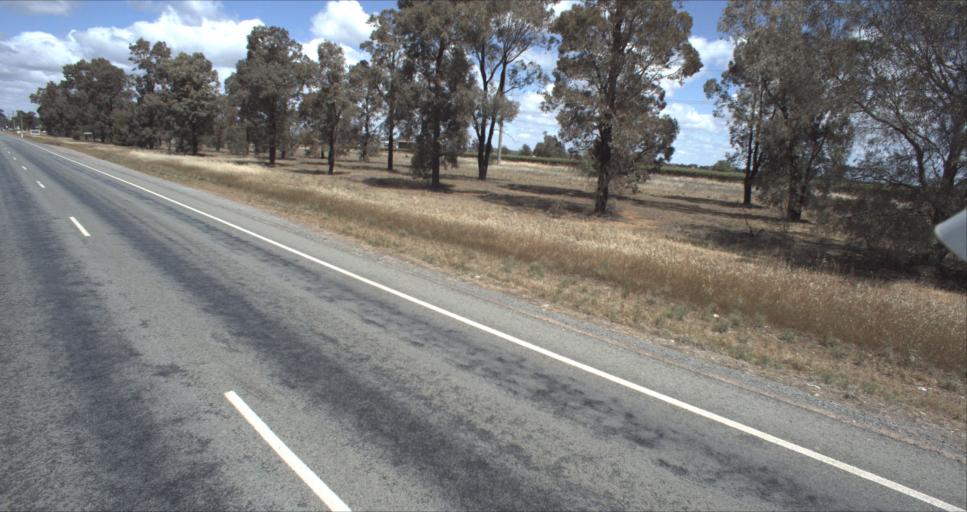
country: AU
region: New South Wales
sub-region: Murrumbidgee Shire
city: Darlington Point
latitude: -34.5070
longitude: 146.1870
